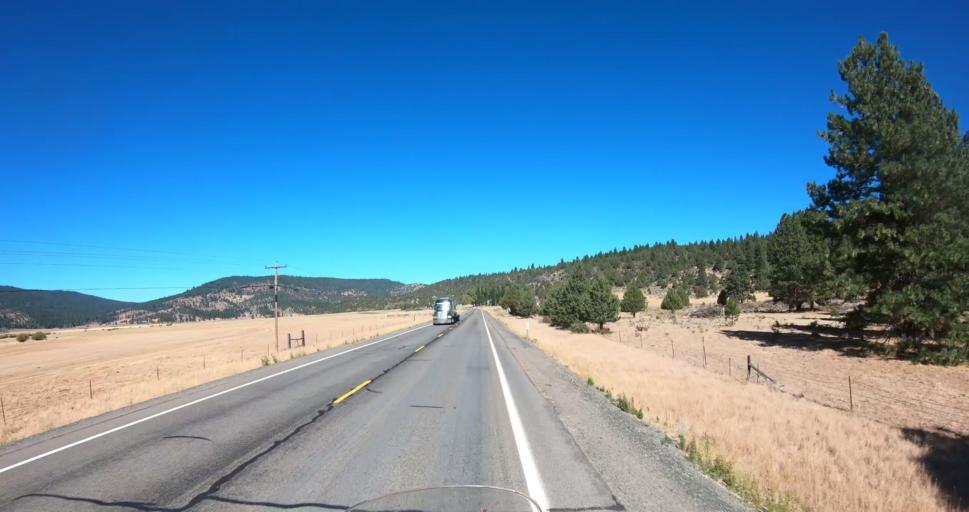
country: US
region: Oregon
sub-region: Lake County
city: Lakeview
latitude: 42.3664
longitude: -120.2970
